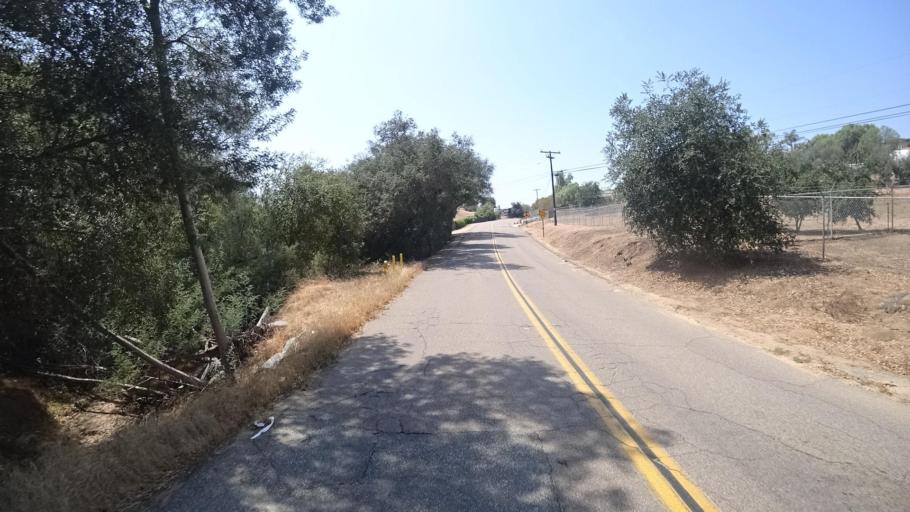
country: US
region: California
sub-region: San Diego County
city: Bonsall
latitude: 33.3148
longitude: -117.2237
